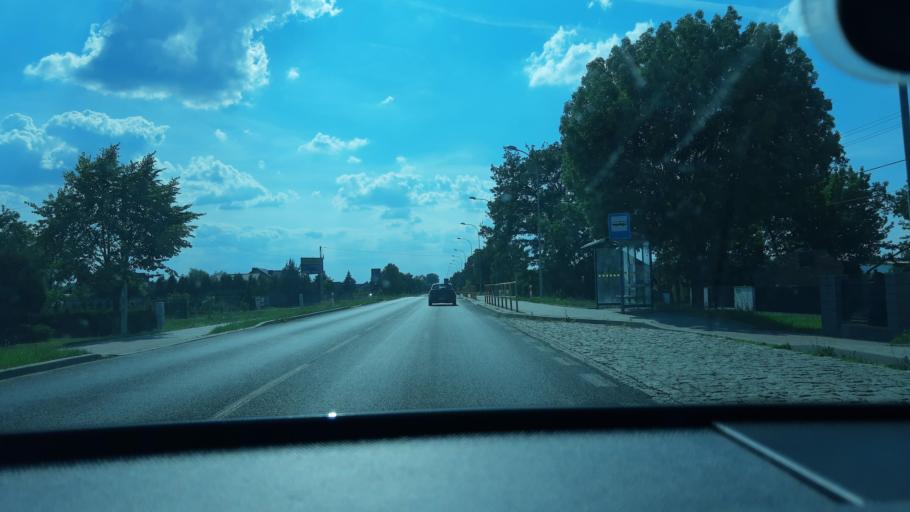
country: PL
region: Lodz Voivodeship
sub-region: Powiat zdunskowolski
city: Zdunska Wola
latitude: 51.6079
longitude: 18.8912
